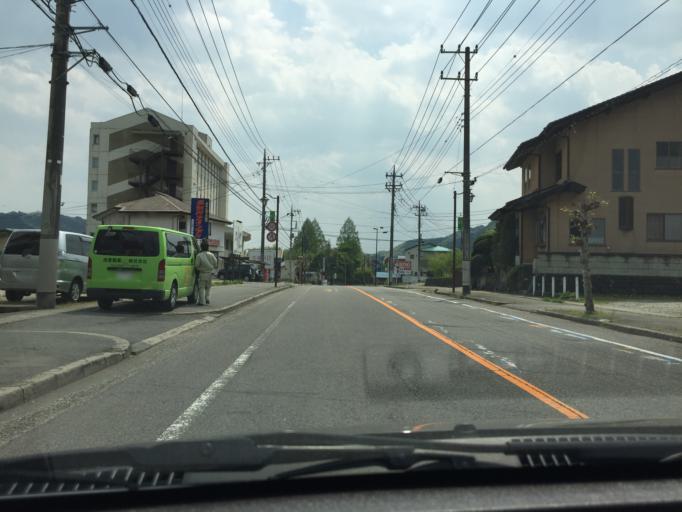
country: JP
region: Tochigi
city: Imaichi
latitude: 36.8307
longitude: 139.7158
